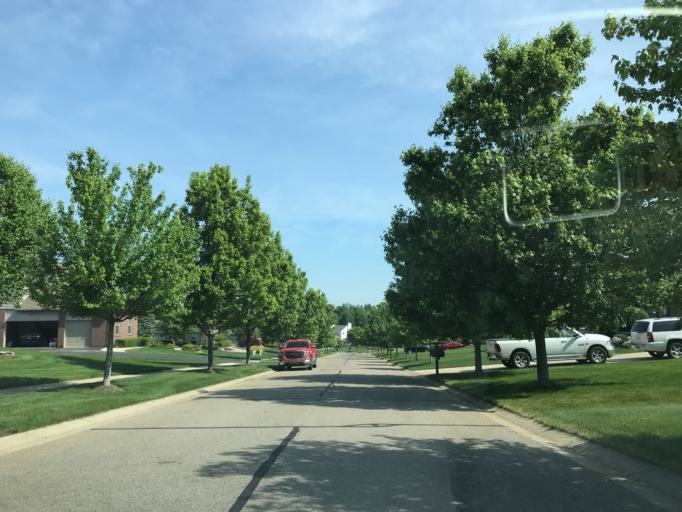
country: US
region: Michigan
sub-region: Oakland County
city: South Lyon
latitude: 42.4794
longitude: -83.6337
